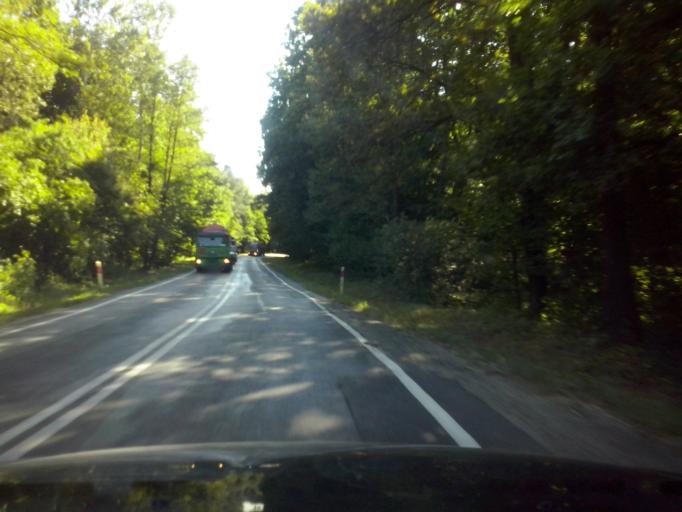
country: PL
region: Swietokrzyskie
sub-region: Powiat kielecki
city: Chmielnik
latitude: 50.6038
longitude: 20.6665
